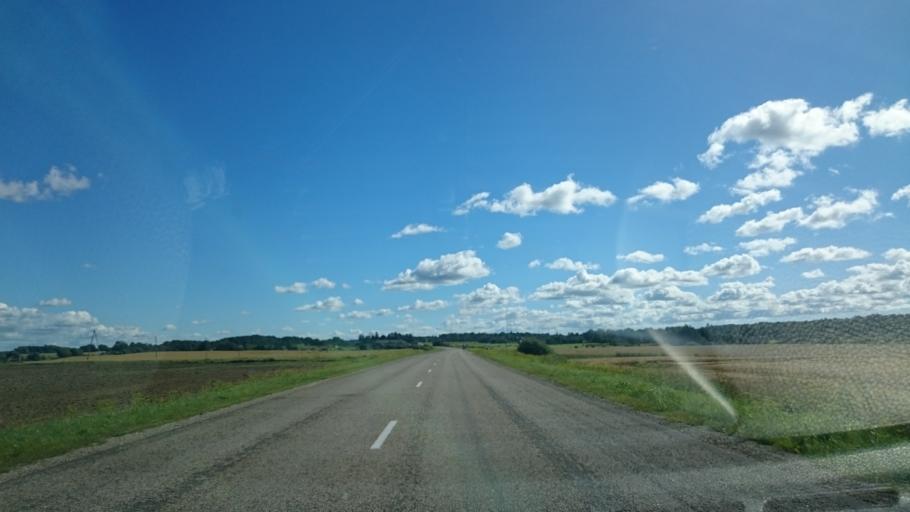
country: LV
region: Aizpute
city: Aizpute
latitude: 56.7534
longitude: 21.6144
